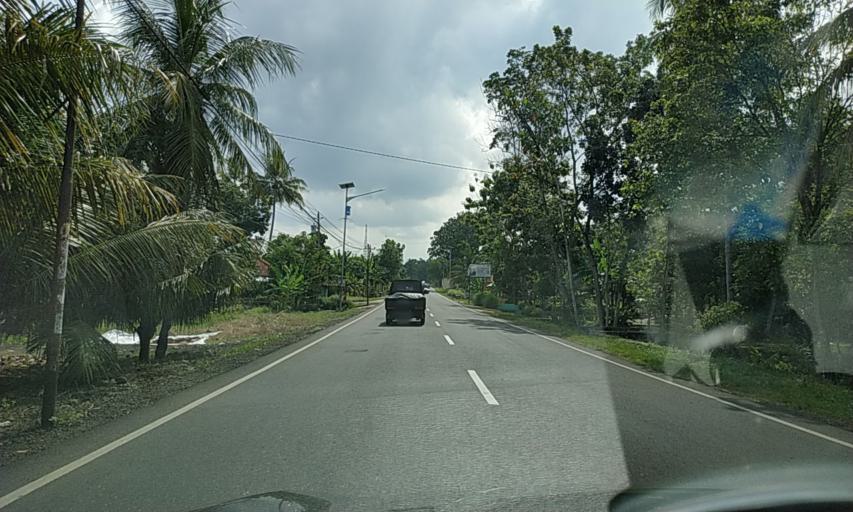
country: ID
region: Central Java
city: Cihandiwung Lor
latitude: -7.3370
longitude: 108.6968
